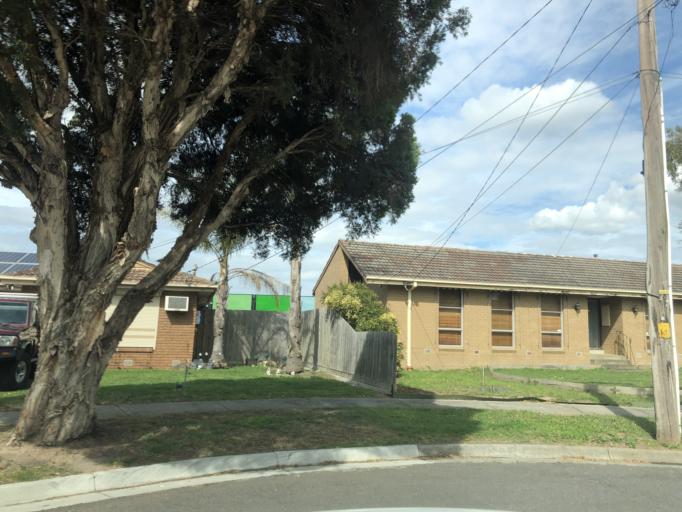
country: AU
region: Victoria
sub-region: Greater Dandenong
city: Noble Park North
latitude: -37.9500
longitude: 145.2029
